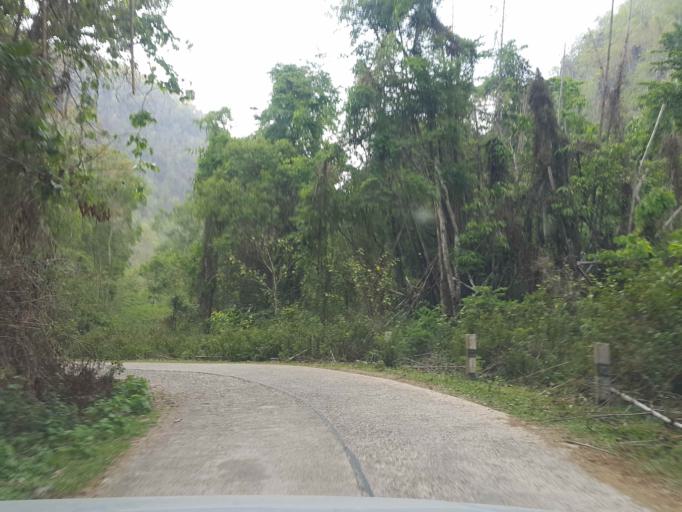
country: TH
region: Chiang Mai
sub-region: Amphoe Chiang Dao
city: Chiang Dao
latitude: 19.3869
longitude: 98.7699
